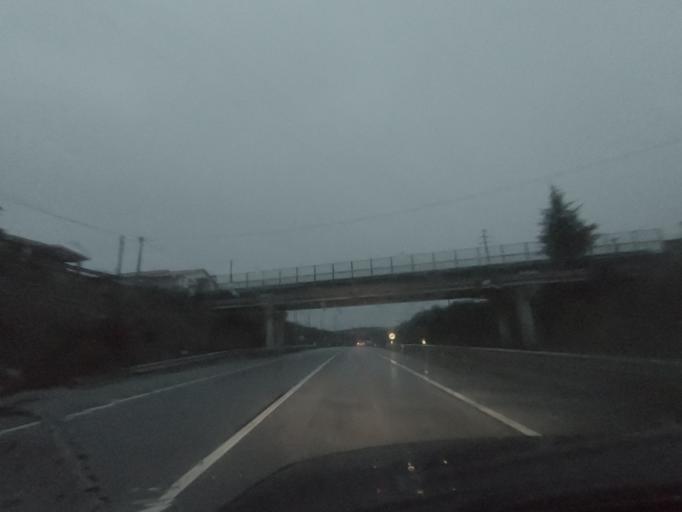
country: PT
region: Vila Real
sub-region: Vila Real
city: Vila Real
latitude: 41.2801
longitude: -7.7026
